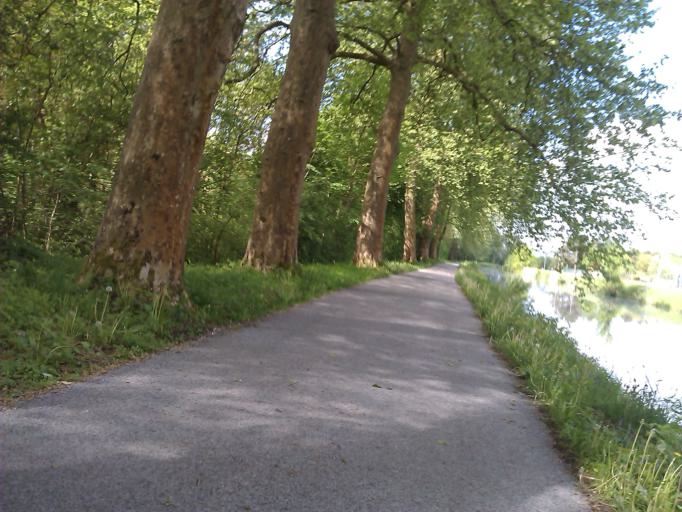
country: FR
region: Franche-Comte
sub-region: Departement du Doubs
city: Roulans
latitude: 47.2892
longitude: 6.1962
